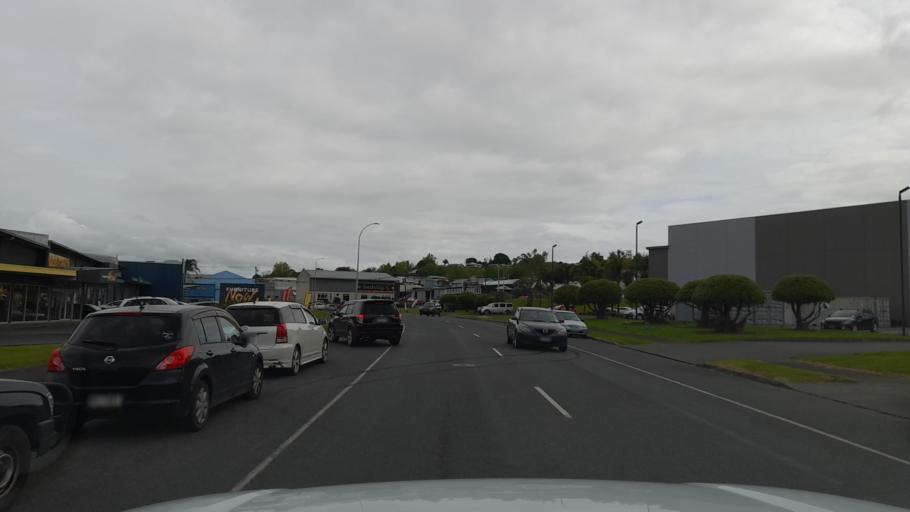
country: NZ
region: Northland
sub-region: Whangarei
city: Whangarei
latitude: -35.7509
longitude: 174.3116
